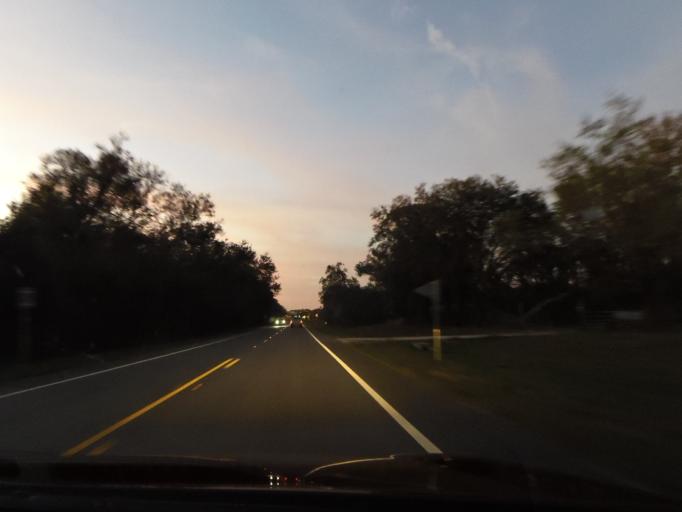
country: US
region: Florida
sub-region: Volusia County
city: De Leon Springs
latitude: 29.2201
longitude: -81.3182
